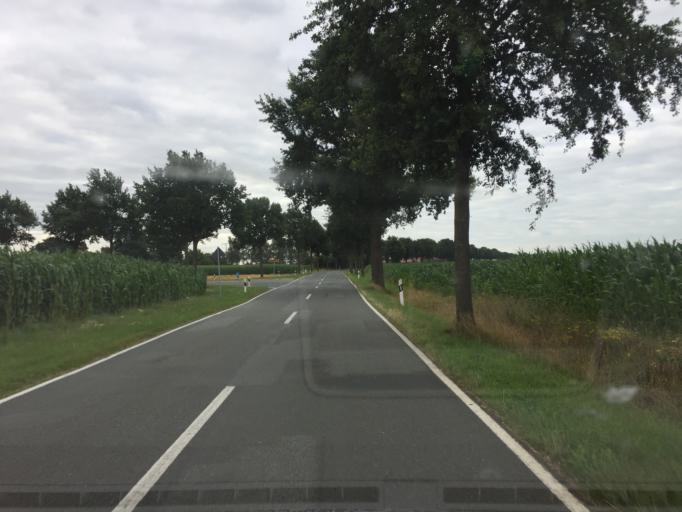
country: DE
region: Lower Saxony
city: Ehrenburg
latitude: 52.7641
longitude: 8.7163
